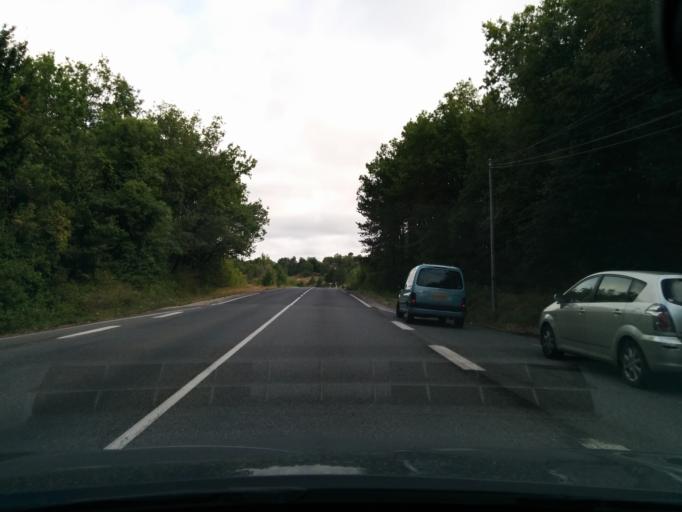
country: FR
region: Midi-Pyrenees
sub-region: Departement du Lot
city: Pradines
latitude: 44.5332
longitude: 1.4683
